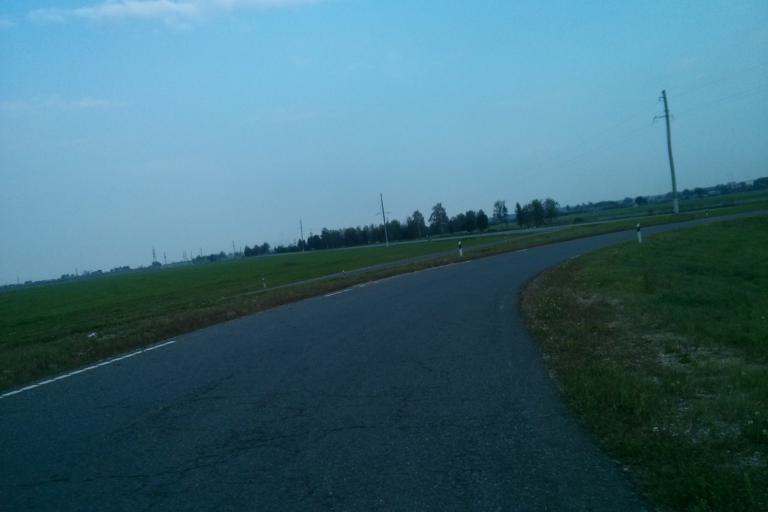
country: BY
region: Minsk
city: Chervyen'
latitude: 53.7256
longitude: 28.3947
